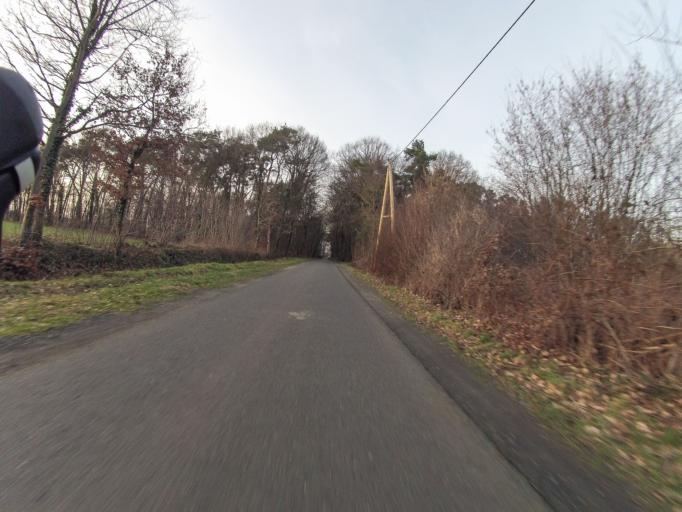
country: DE
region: North Rhine-Westphalia
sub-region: Regierungsbezirk Munster
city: Steinfurt
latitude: 52.1750
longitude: 7.3332
